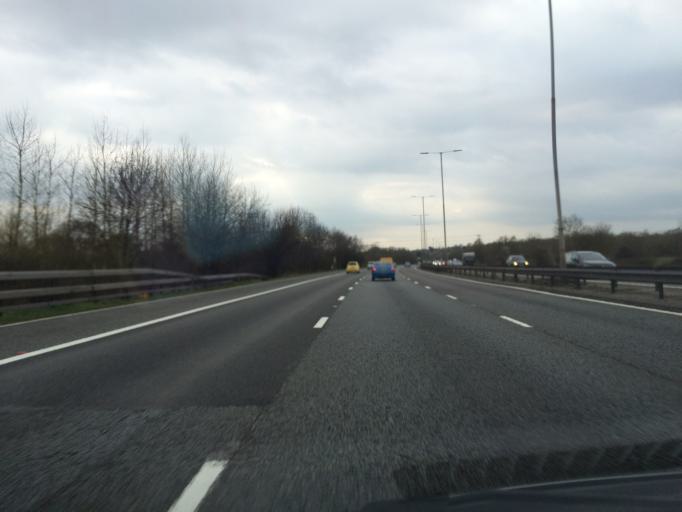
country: GB
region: England
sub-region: Wokingham
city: Lower Earley
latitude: 51.4199
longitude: -0.9142
